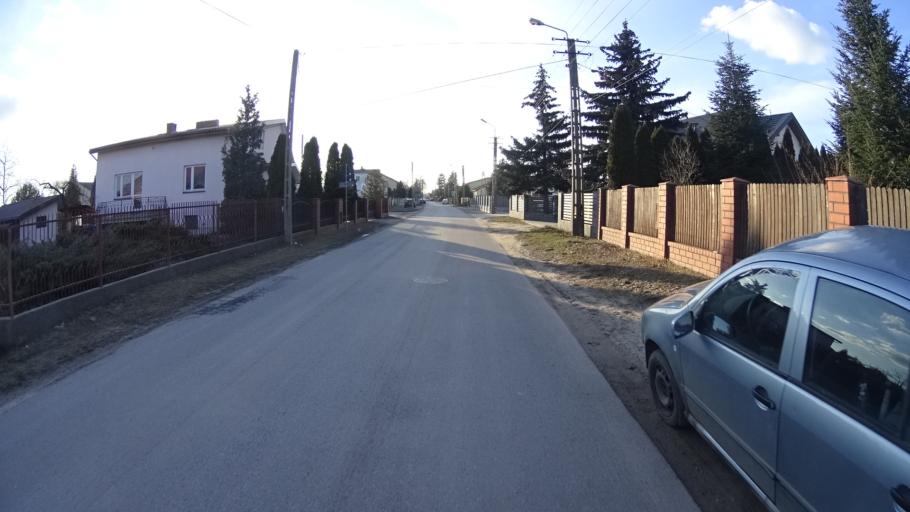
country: PL
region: Masovian Voivodeship
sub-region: Powiat warszawski zachodni
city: Truskaw
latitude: 52.2593
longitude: 20.7598
